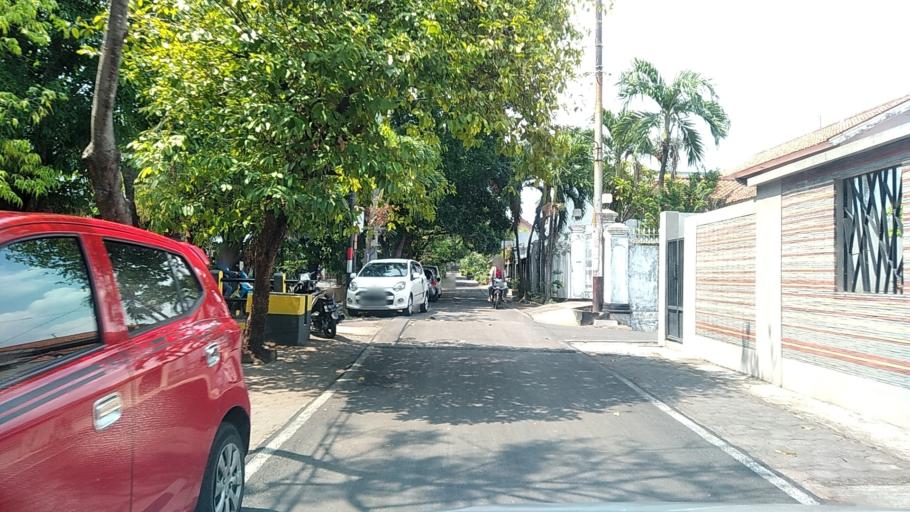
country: ID
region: Central Java
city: Semarang
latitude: -7.0036
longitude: 110.4387
